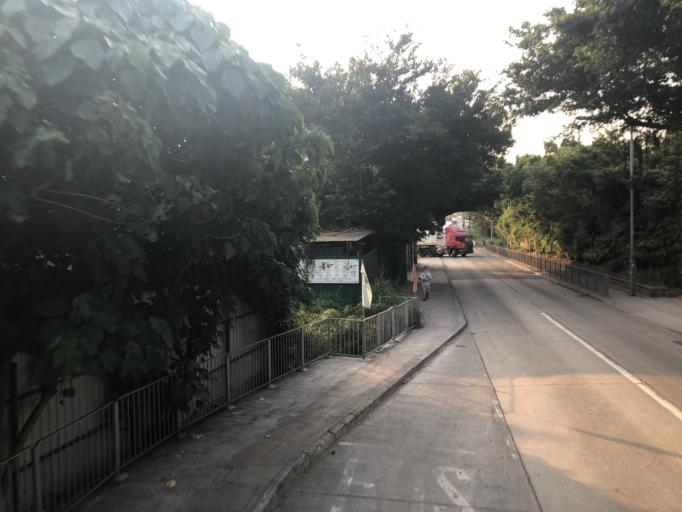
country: HK
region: Yuen Long
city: Yuen Long Kau Hui
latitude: 22.4646
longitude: 113.9863
